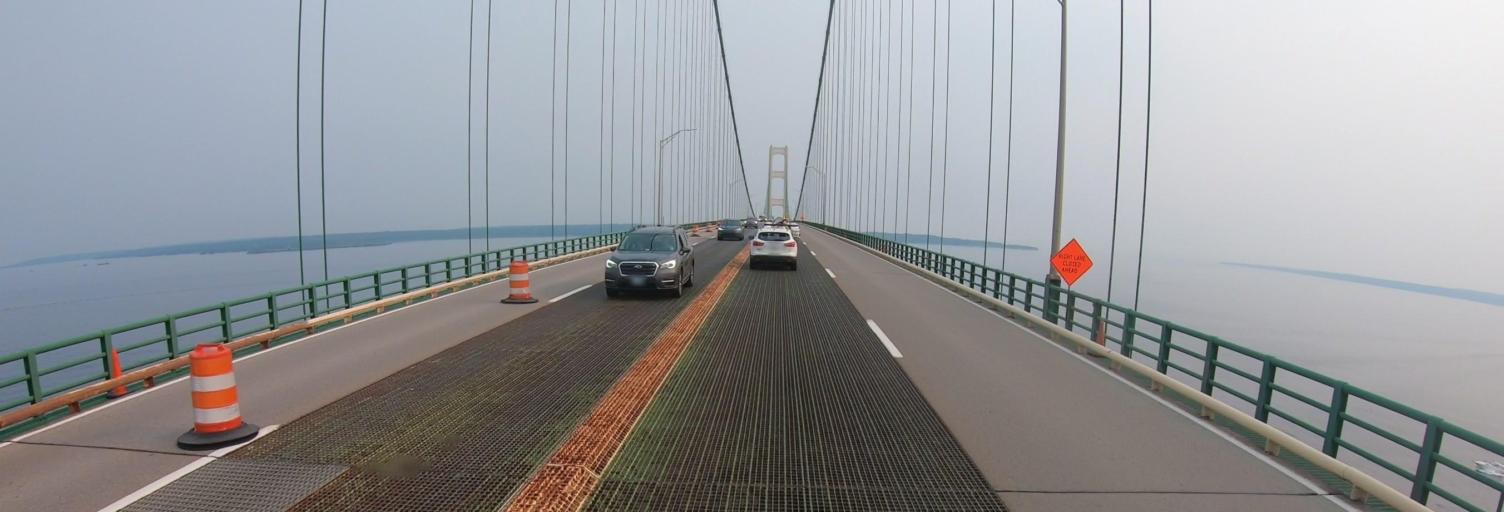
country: US
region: Michigan
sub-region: Mackinac County
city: Saint Ignace
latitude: 45.8113
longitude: -84.7267
